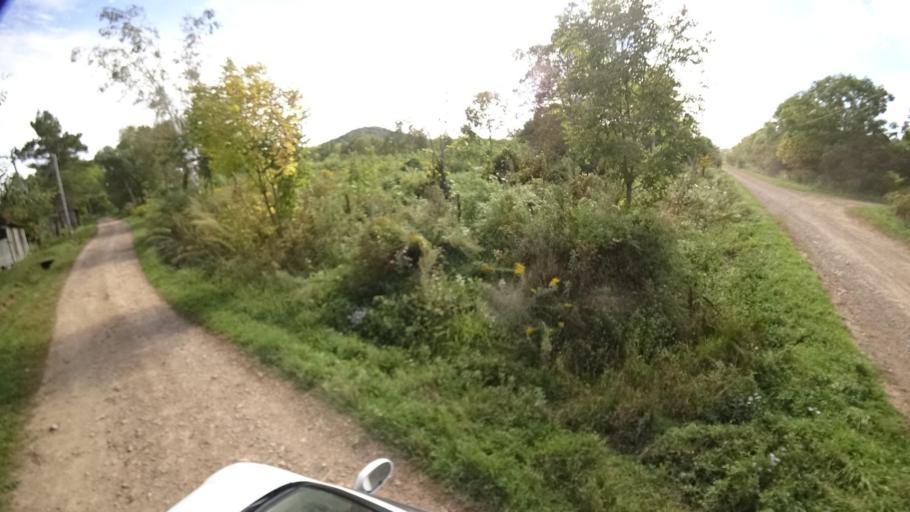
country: RU
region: Primorskiy
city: Yakovlevka
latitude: 44.3899
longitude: 133.6060
